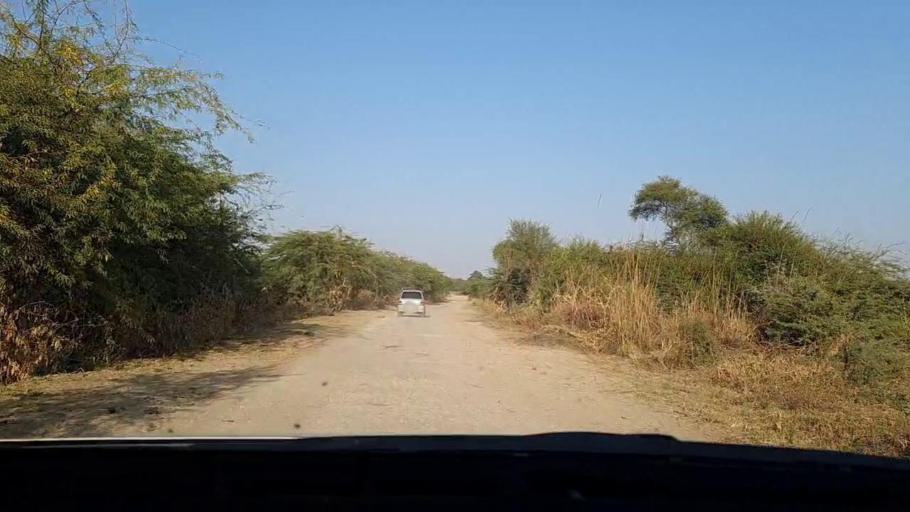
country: PK
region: Sindh
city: Tando Mittha Khan
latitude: 25.8564
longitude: 69.3125
